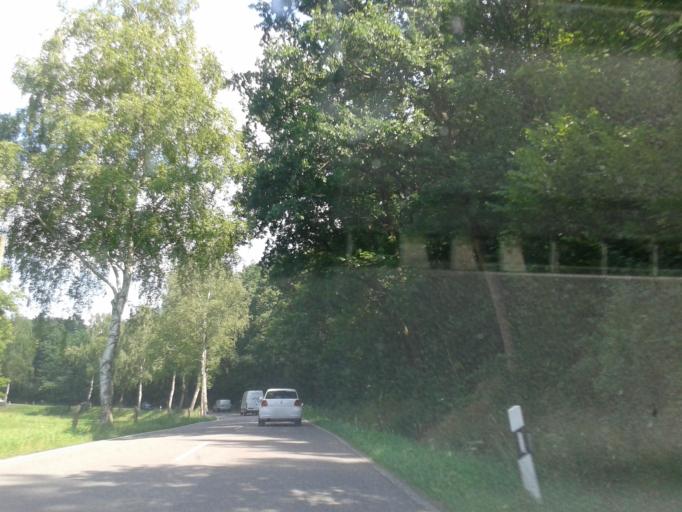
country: DE
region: Saxony
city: Reinsberg
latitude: 51.0452
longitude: 13.4288
